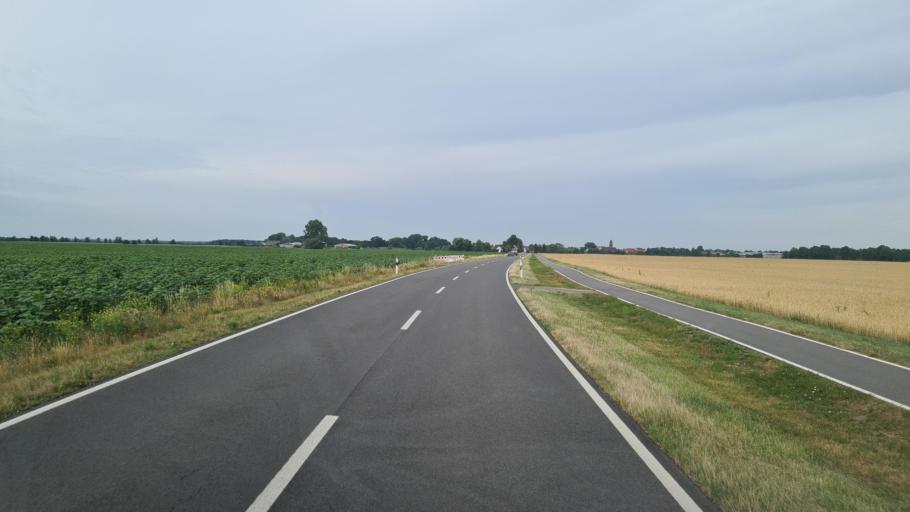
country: DE
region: Saxony-Anhalt
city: Jessen
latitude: 51.7711
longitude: 12.9202
